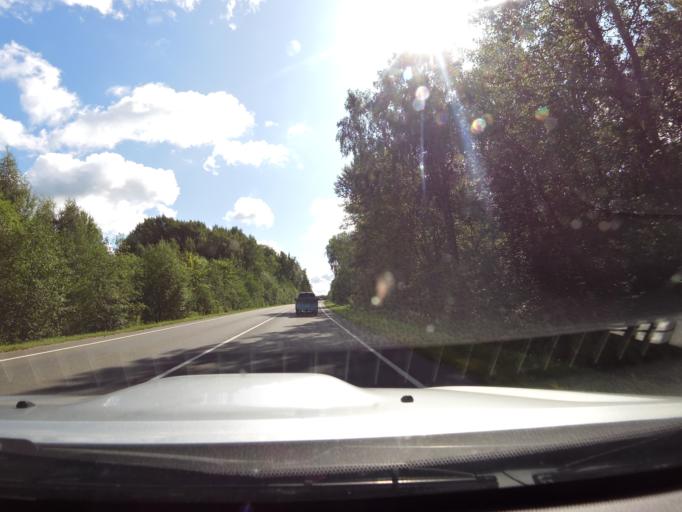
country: LT
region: Utenos apskritis
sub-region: Utena
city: Utena
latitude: 55.4875
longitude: 25.6309
